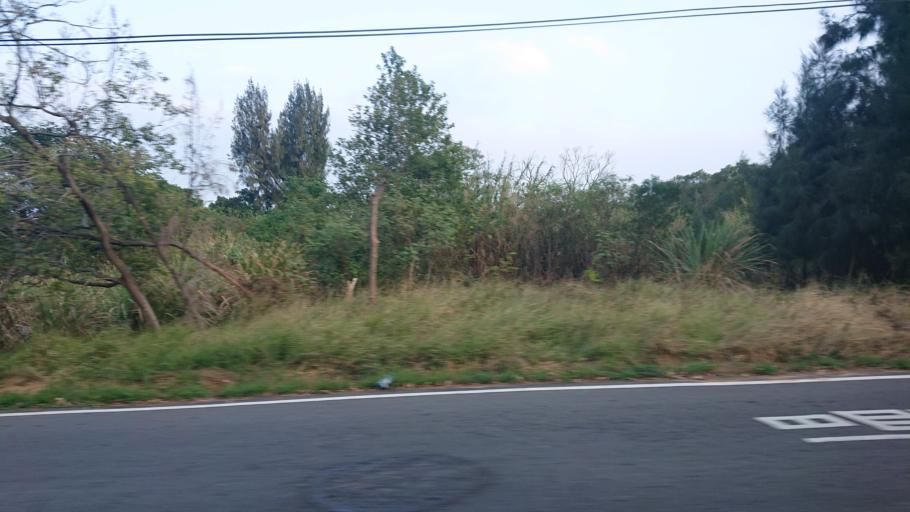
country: CN
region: Fujian
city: Dadeng
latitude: 24.4849
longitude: 118.4388
